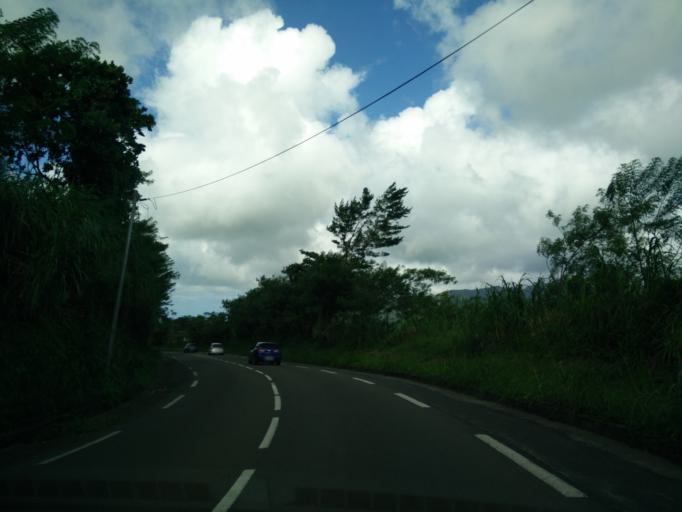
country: MQ
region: Martinique
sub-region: Martinique
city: Le Morne-Rouge
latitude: 14.7924
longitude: -61.1372
